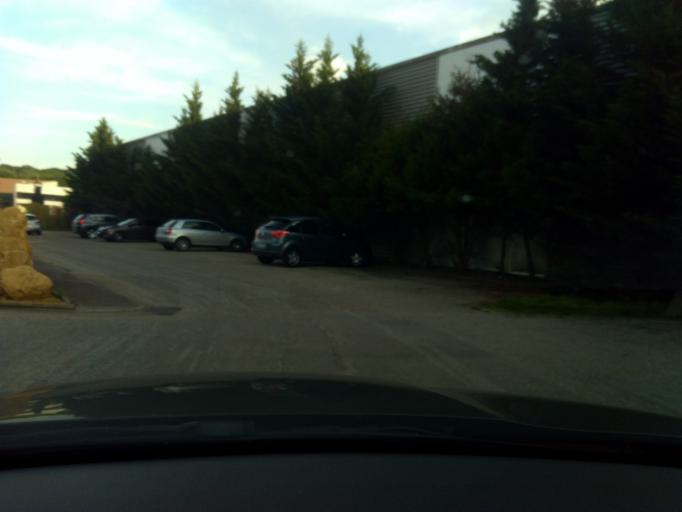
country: FR
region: Lorraine
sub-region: Departement de la Moselle
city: Jouy-aux-Arches
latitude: 49.0760
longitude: 6.0970
